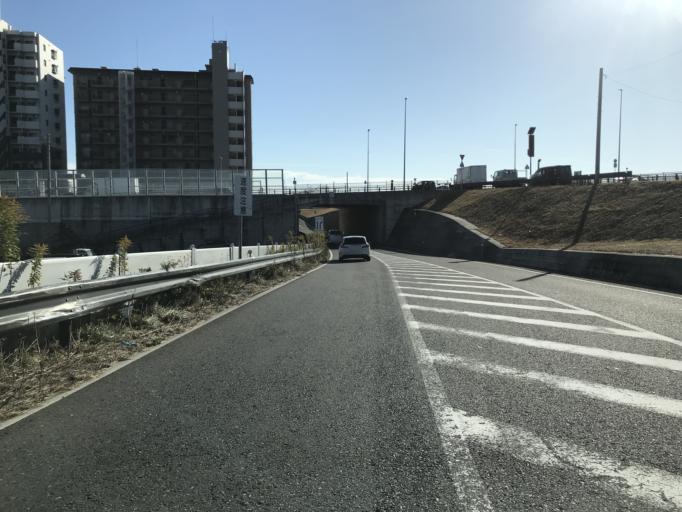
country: JP
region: Aichi
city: Kanie
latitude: 35.1248
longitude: 136.8389
